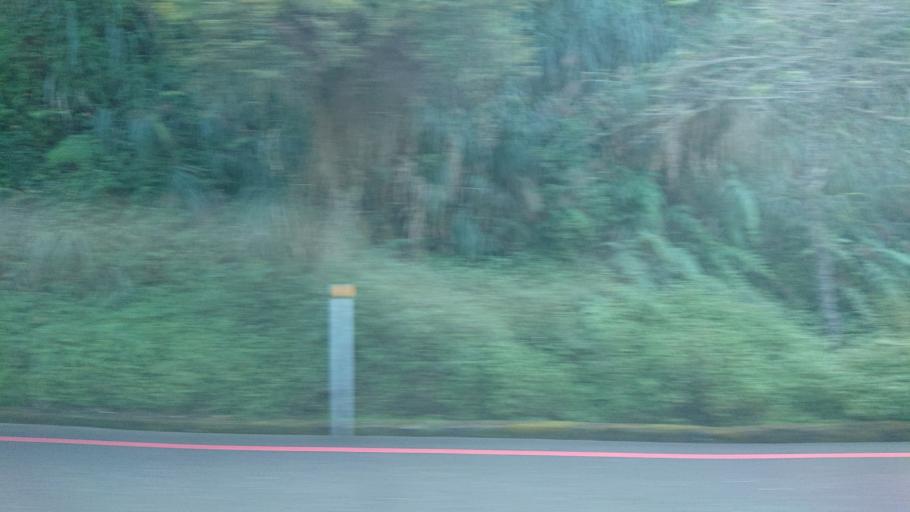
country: TW
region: Taiwan
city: Lugu
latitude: 23.5069
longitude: 120.7966
